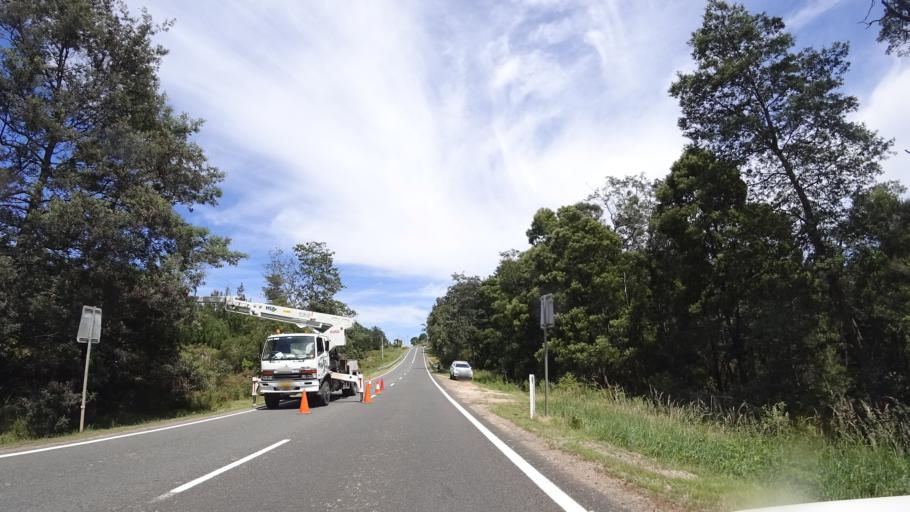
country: AU
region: Tasmania
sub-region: Dorset
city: Scottsdale
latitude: -41.1680
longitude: 147.7537
